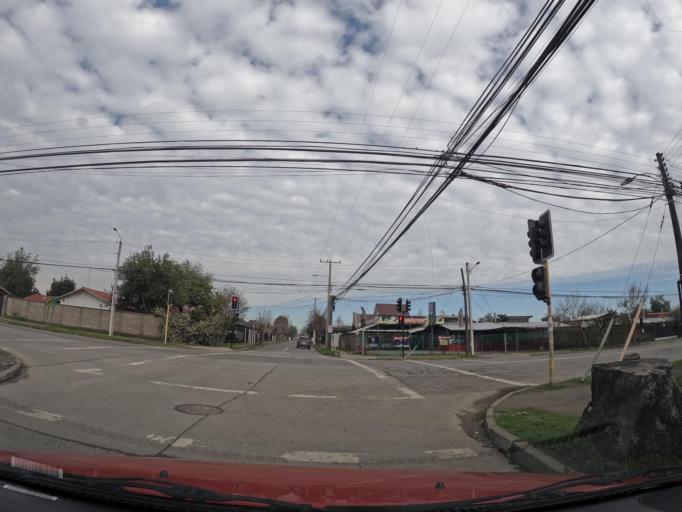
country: CL
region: Maule
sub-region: Provincia de Linares
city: Linares
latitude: -35.8383
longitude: -71.6028
